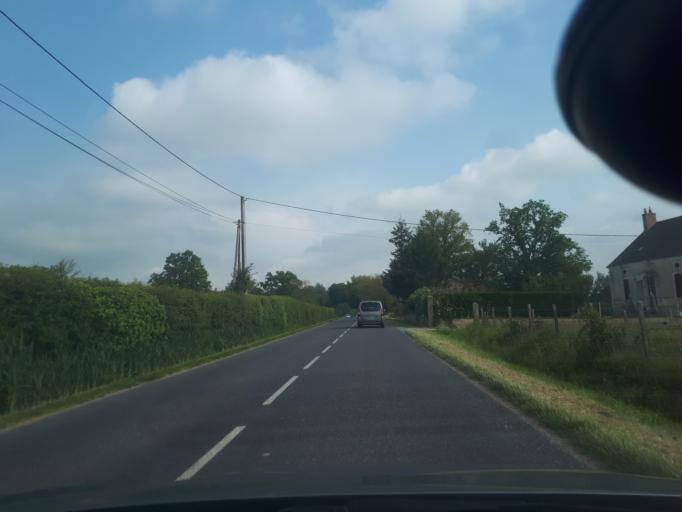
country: FR
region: Auvergne
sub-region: Departement de l'Allier
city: Saint-Gerand-le-Puy
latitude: 46.3407
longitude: 3.5797
